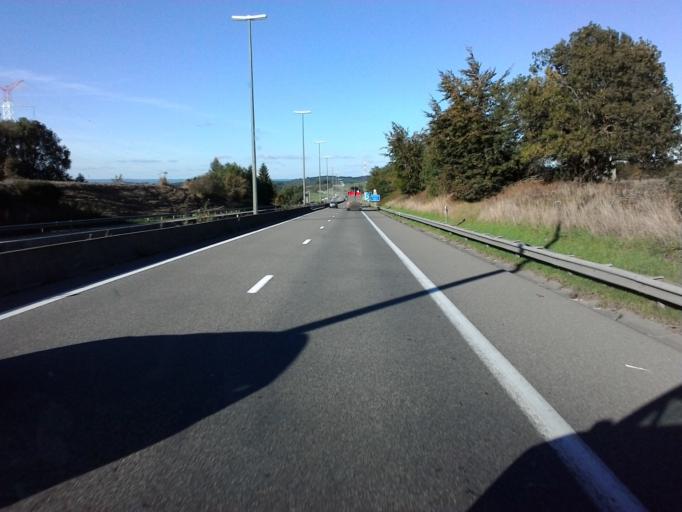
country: BE
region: Wallonia
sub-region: Province du Luxembourg
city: Bastogne
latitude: 50.0092
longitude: 5.6885
